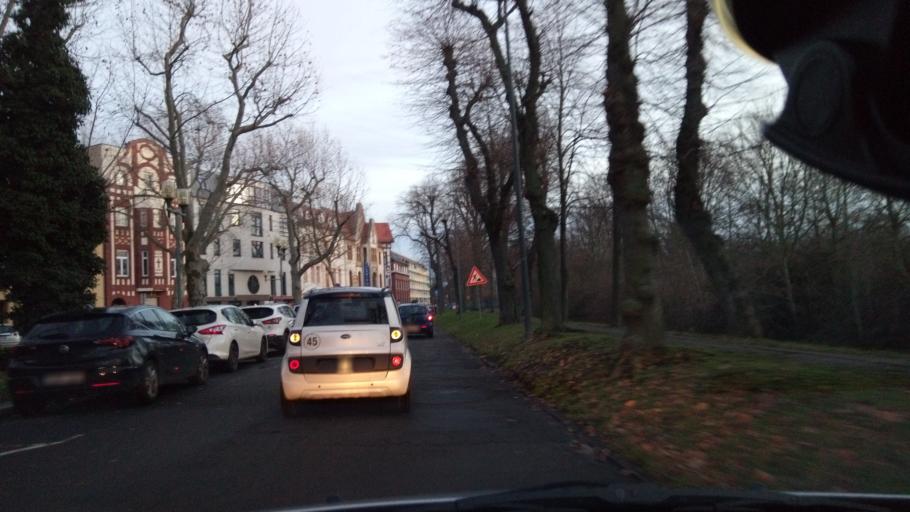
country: DE
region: Saxony
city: Bitterfeld-Wolfen
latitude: 51.6224
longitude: 12.3299
